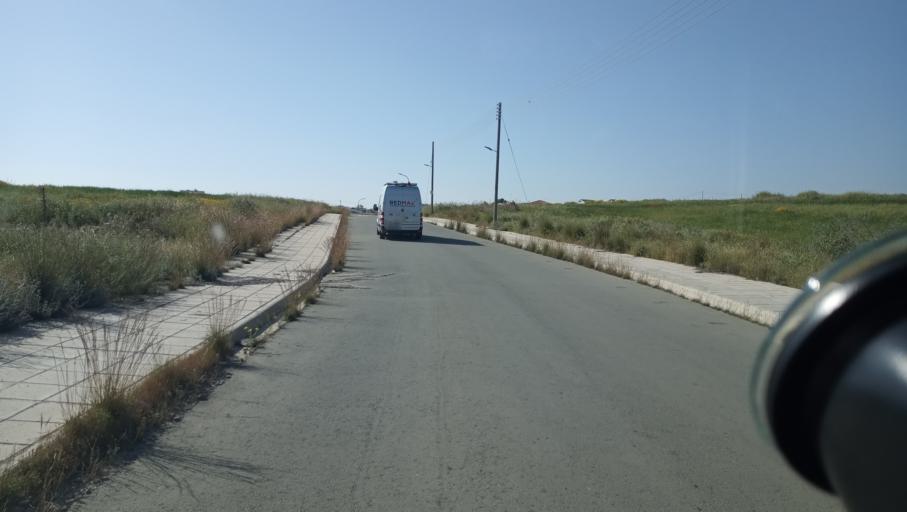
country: CY
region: Lefkosia
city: Geri
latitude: 35.0791
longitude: 33.3938
